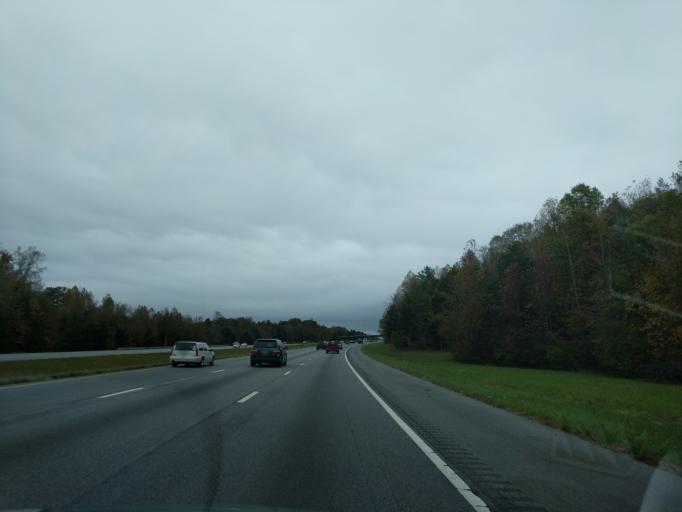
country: US
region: North Carolina
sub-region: Randolph County
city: Trinity
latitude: 35.8828
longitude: -79.9972
